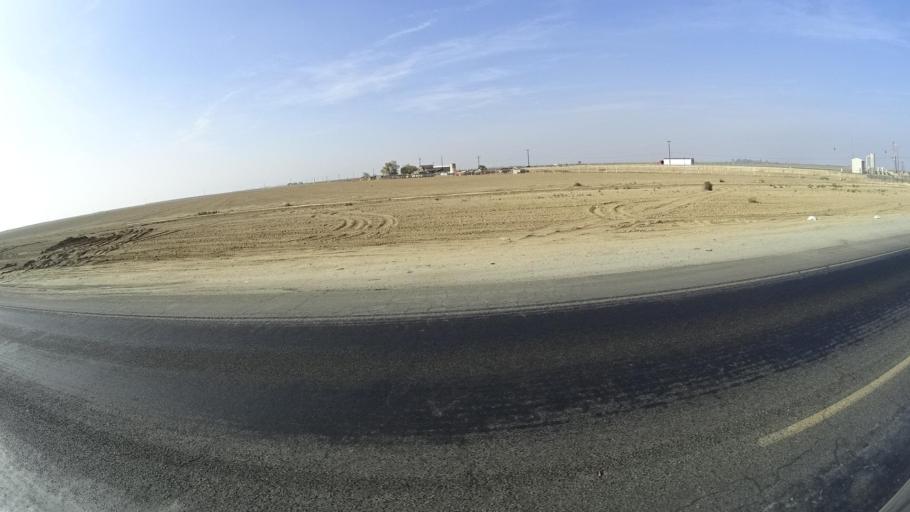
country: US
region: California
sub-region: Kern County
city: McFarland
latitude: 35.7163
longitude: -119.1603
